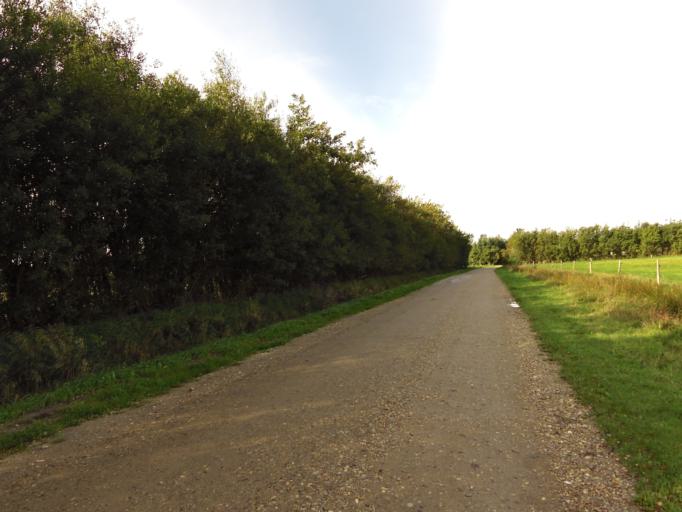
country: DK
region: South Denmark
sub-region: Varde Kommune
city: Oksbol
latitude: 55.5536
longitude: 8.2224
